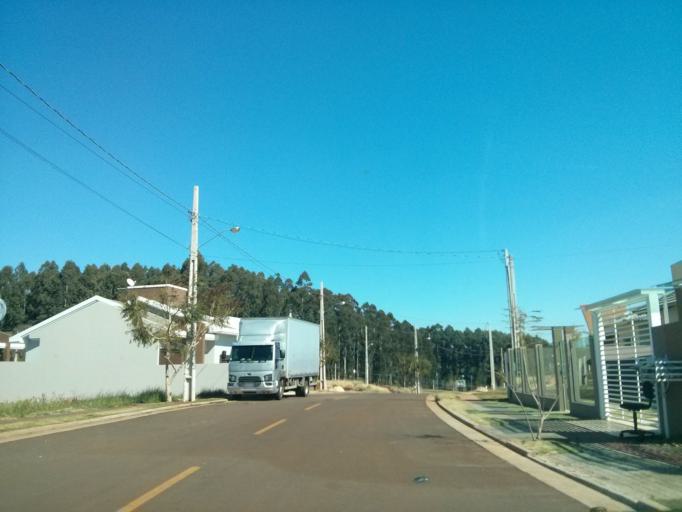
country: BR
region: Santa Catarina
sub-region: Chapeco
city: Chapeco
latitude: -27.0908
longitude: -52.7127
